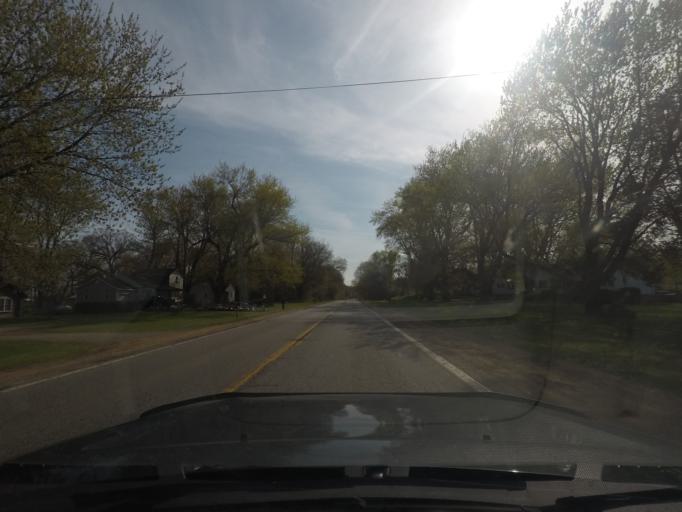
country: US
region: Michigan
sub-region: Berrien County
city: Buchanan
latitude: 41.7966
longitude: -86.4153
